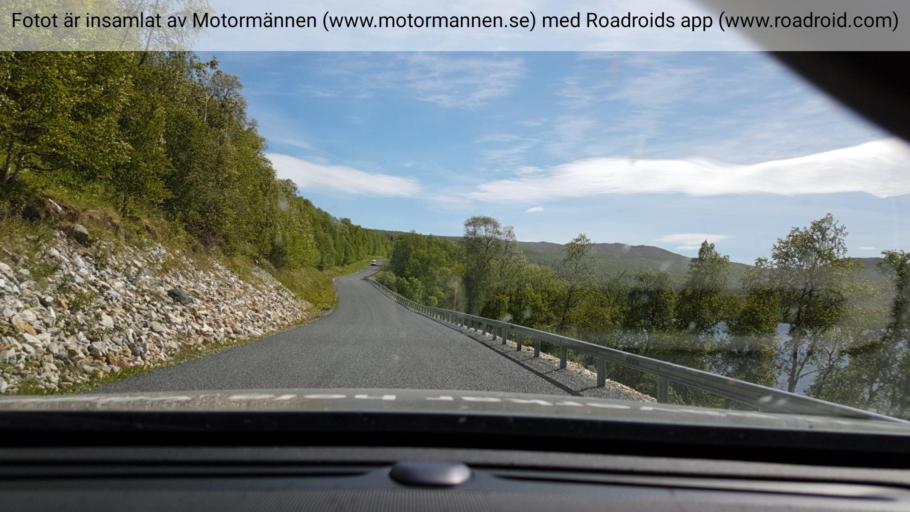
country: SE
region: Vaesterbotten
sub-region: Vilhelmina Kommun
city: Sjoberg
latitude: 65.3240
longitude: 15.2630
